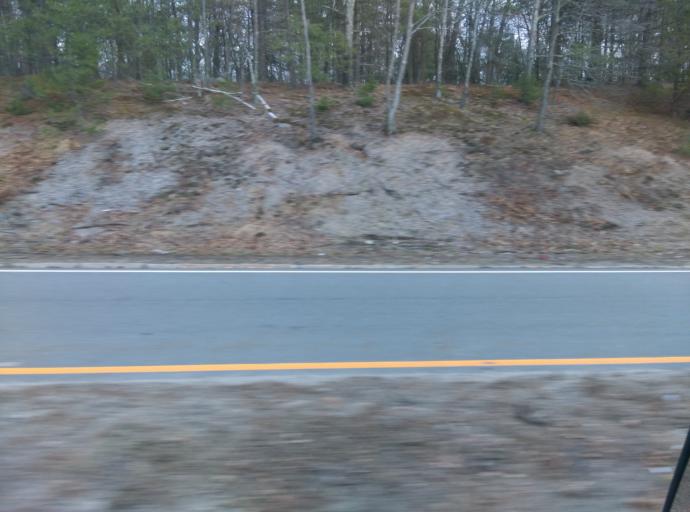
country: US
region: Massachusetts
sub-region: Middlesex County
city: Tewksbury
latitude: 42.6437
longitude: -71.2337
